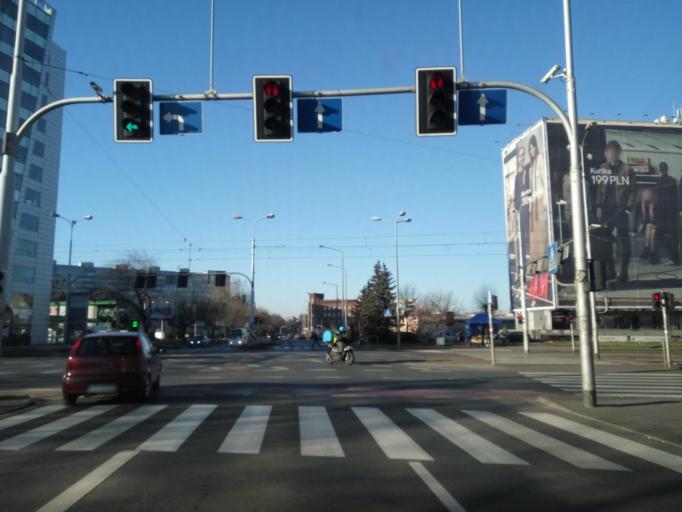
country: PL
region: Lower Silesian Voivodeship
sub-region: Powiat wroclawski
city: Wroclaw
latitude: 51.0993
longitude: 17.0274
